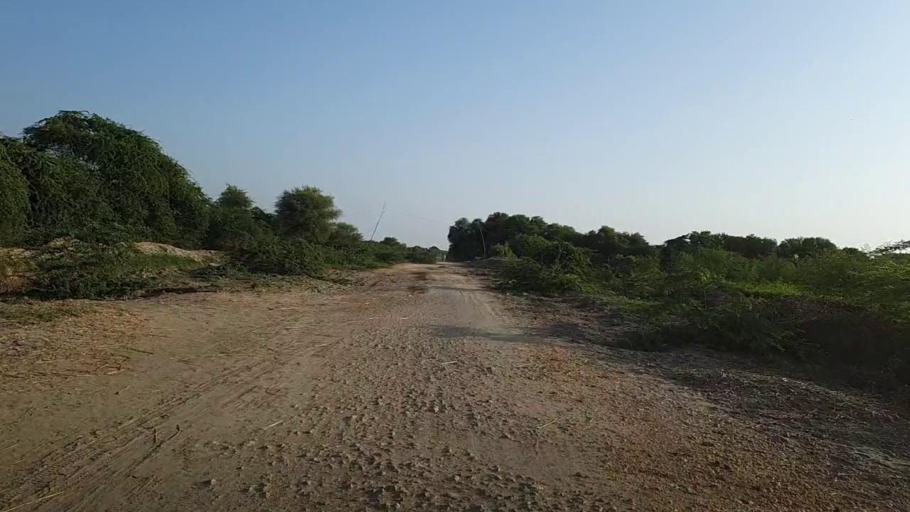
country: PK
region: Sindh
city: Kario
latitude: 24.7219
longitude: 68.6673
